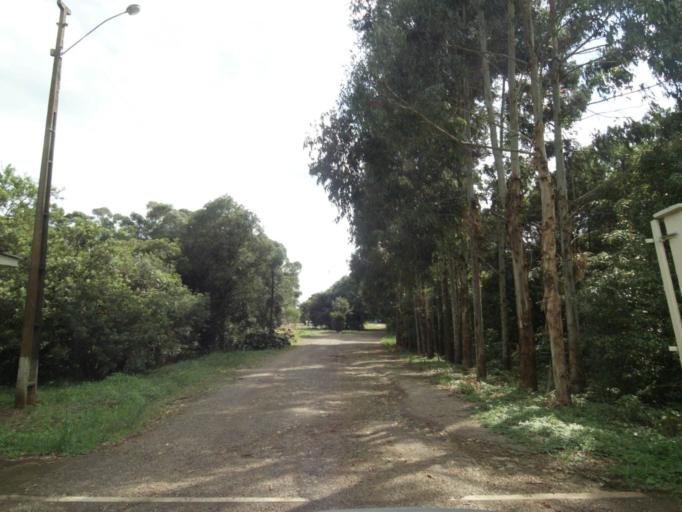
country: BR
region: Rio Grande do Sul
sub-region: Lagoa Vermelha
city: Lagoa Vermelha
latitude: -28.2224
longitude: -51.5110
